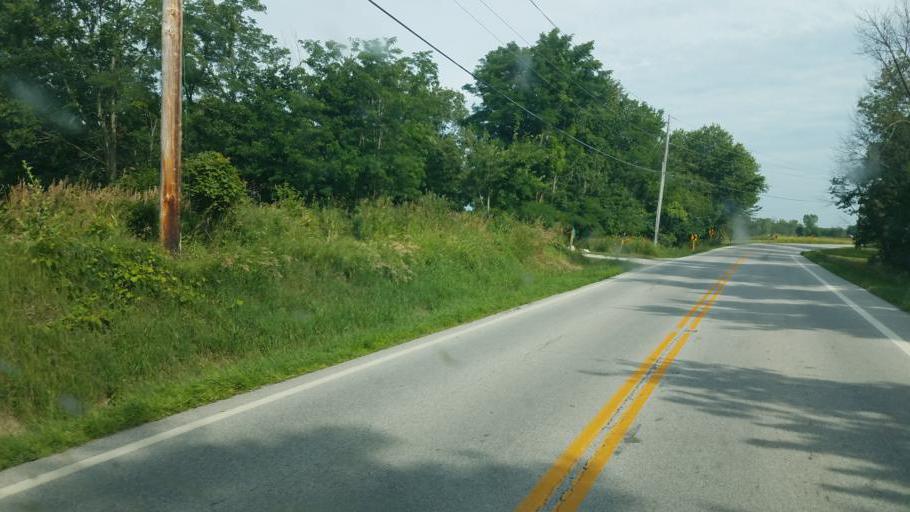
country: US
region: Ohio
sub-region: Medina County
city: Lodi
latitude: 41.0660
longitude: -82.0241
